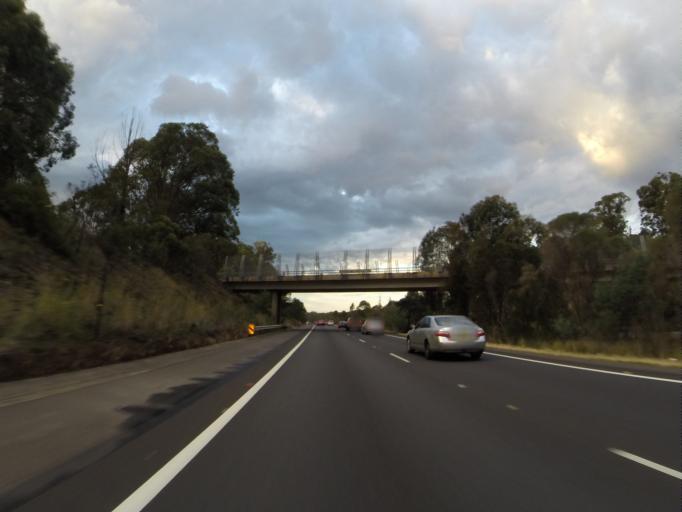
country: AU
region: New South Wales
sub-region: Wollondilly
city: Douglas Park
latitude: -34.1975
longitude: 150.7072
